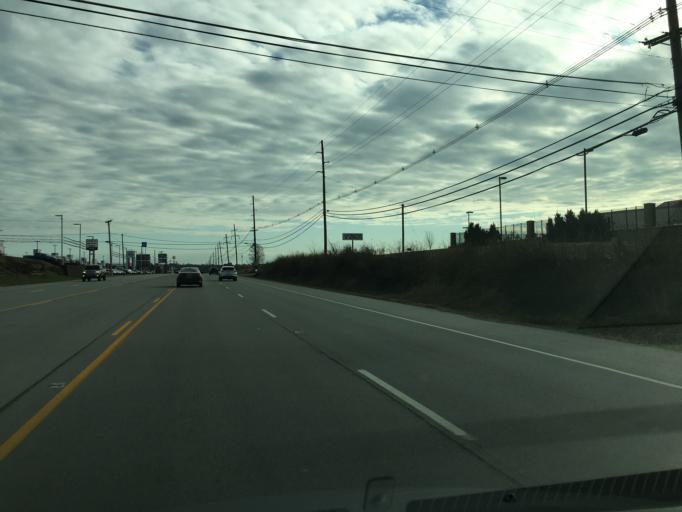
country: US
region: Kentucky
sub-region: Franklin County
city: Frankfort
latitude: 38.1848
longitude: -84.8188
